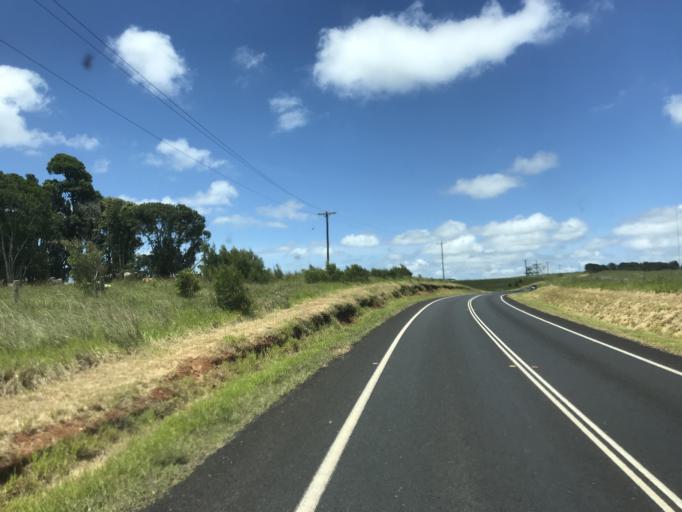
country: AU
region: Queensland
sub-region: Tablelands
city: Ravenshoe
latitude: -17.4913
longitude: 145.4738
